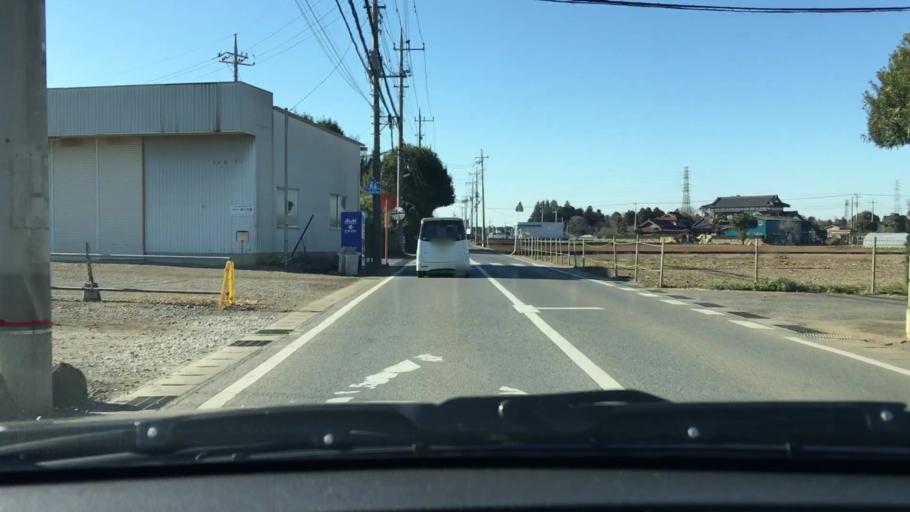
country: JP
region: Chiba
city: Shisui
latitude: 35.6924
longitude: 140.3034
